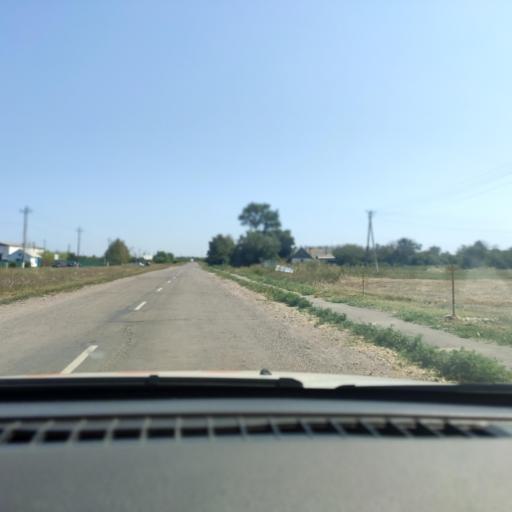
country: RU
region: Voronezj
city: Imeni Pervogo Maya
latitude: 50.7182
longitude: 39.3850
